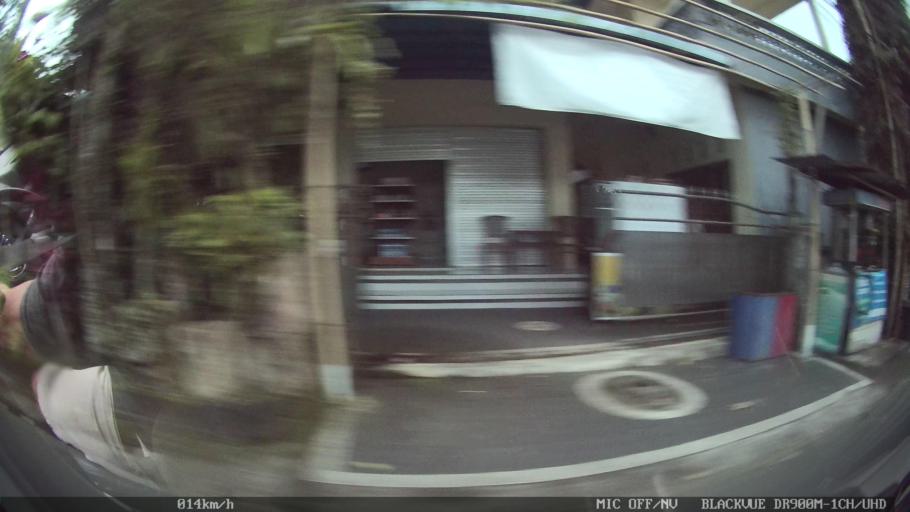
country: ID
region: Bali
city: Bunutan
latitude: -8.4824
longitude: 115.2580
